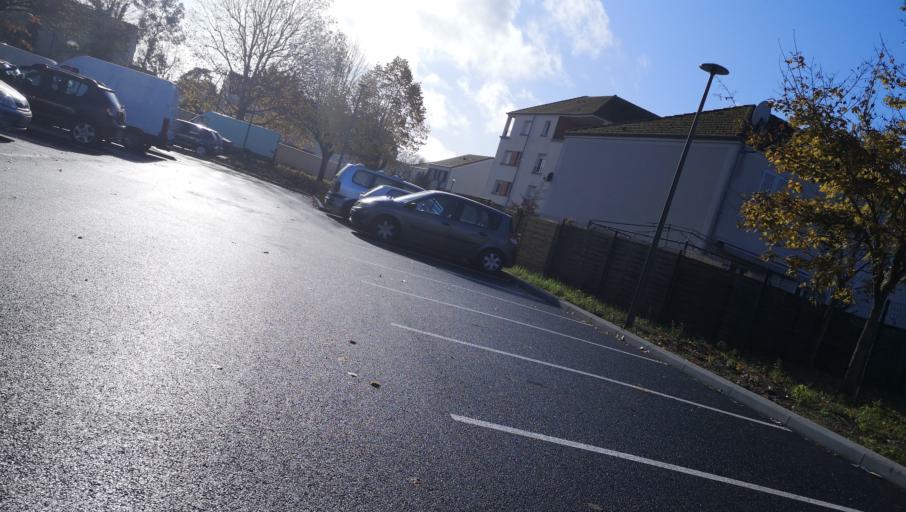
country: FR
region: Centre
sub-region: Departement du Loiret
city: Saint-Jean-le-Blanc
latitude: 47.9069
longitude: 1.9340
